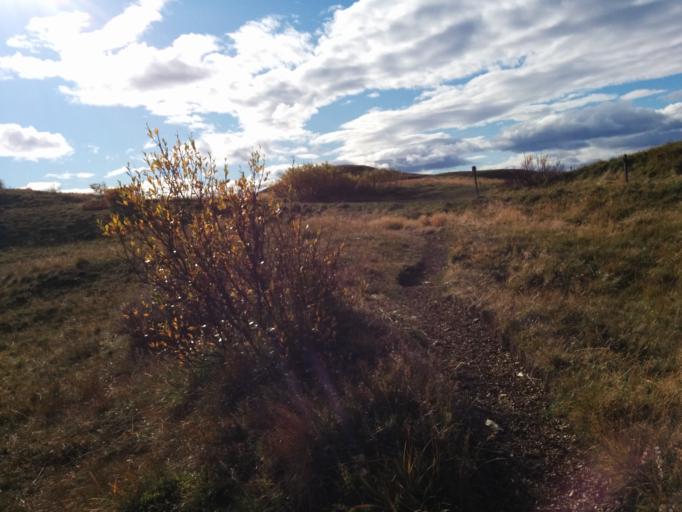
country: IS
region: Northeast
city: Laugar
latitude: 65.5776
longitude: -16.9610
